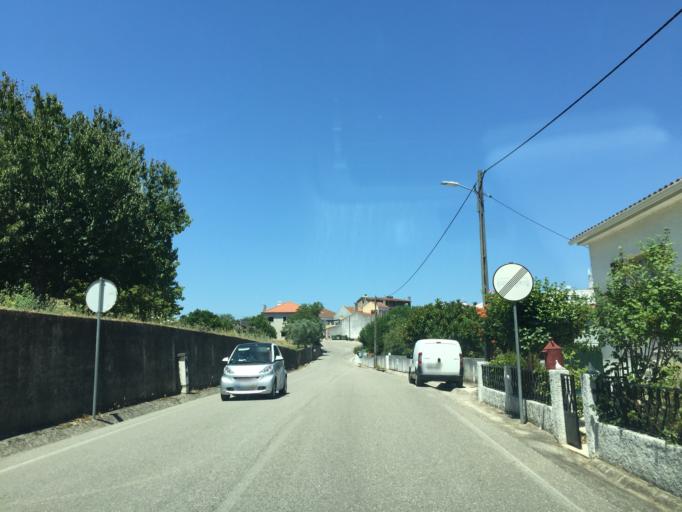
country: PT
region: Santarem
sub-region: Ferreira do Zezere
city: Ferreira do Zezere
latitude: 39.5982
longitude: -8.2992
